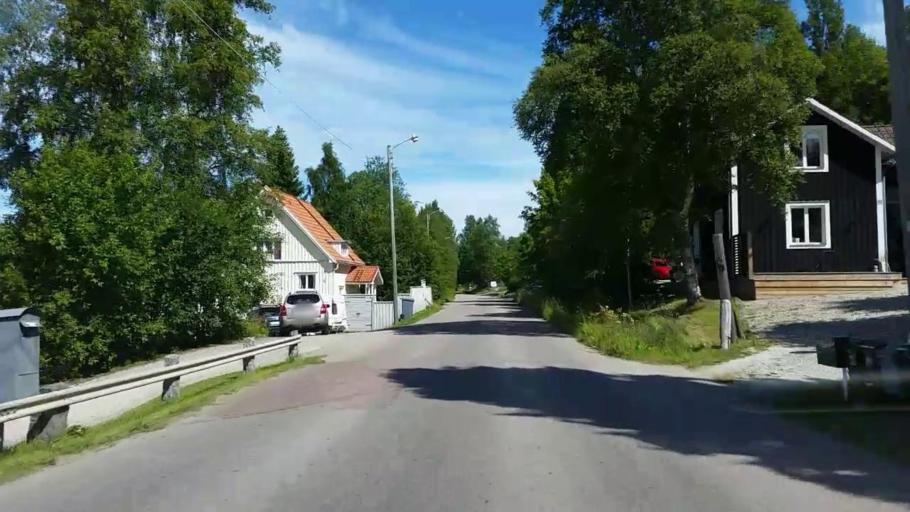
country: SE
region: Dalarna
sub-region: Rattviks Kommun
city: Raettvik
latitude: 60.8823
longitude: 15.1272
